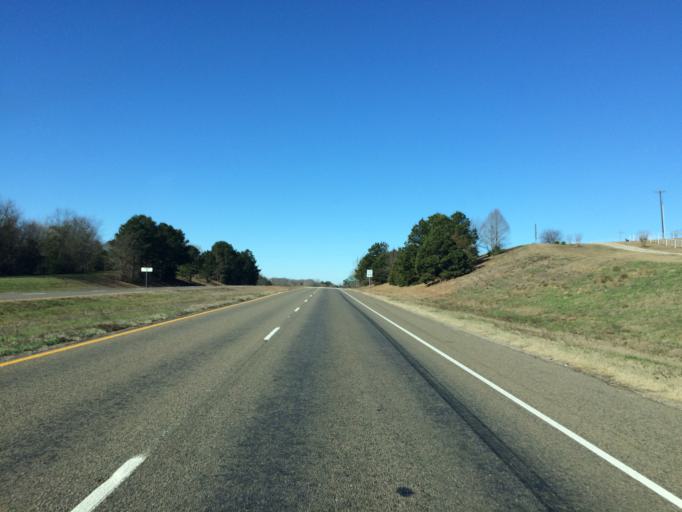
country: US
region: Texas
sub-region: Wood County
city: Hawkins
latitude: 32.6164
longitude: -95.3133
